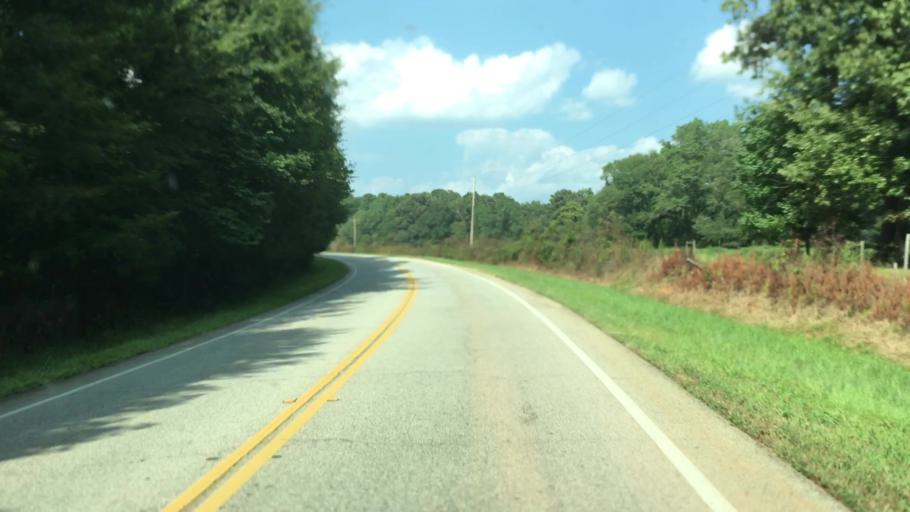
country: US
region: Georgia
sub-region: Butts County
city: Indian Springs
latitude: 33.1404
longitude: -83.8548
